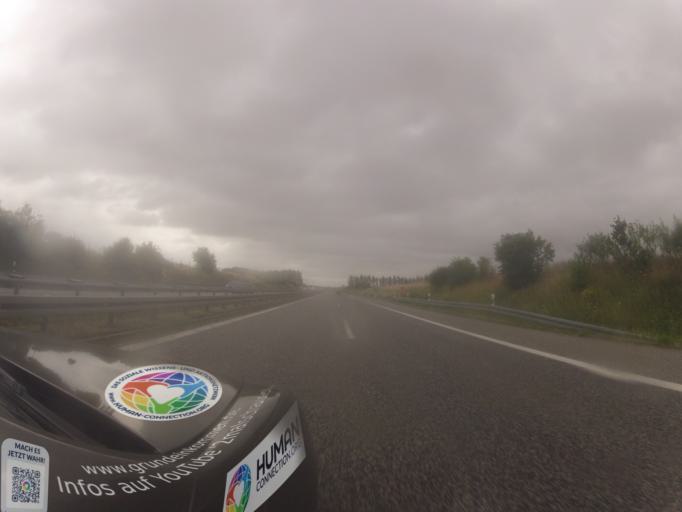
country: DE
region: Brandenburg
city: Schonfeld
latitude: 53.4514
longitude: 13.9781
